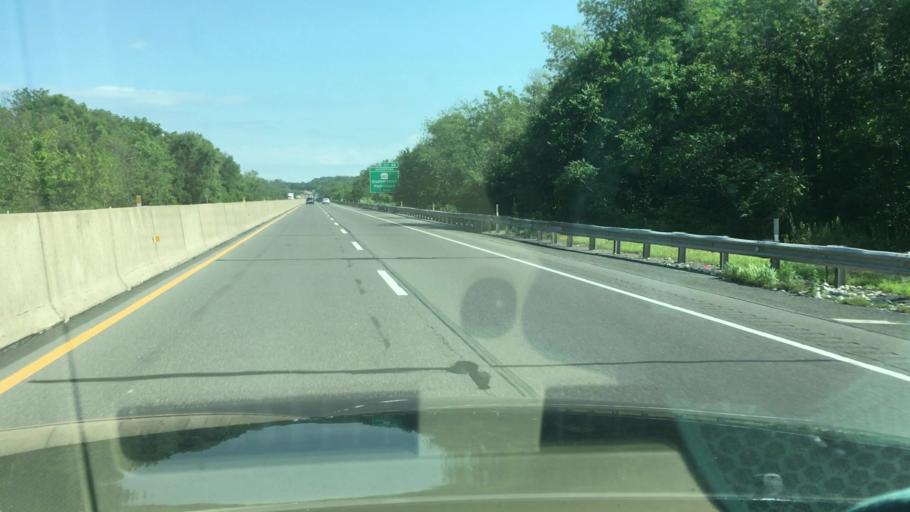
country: US
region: Pennsylvania
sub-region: Bucks County
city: Spinnerstown
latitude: 40.4066
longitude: -75.4129
